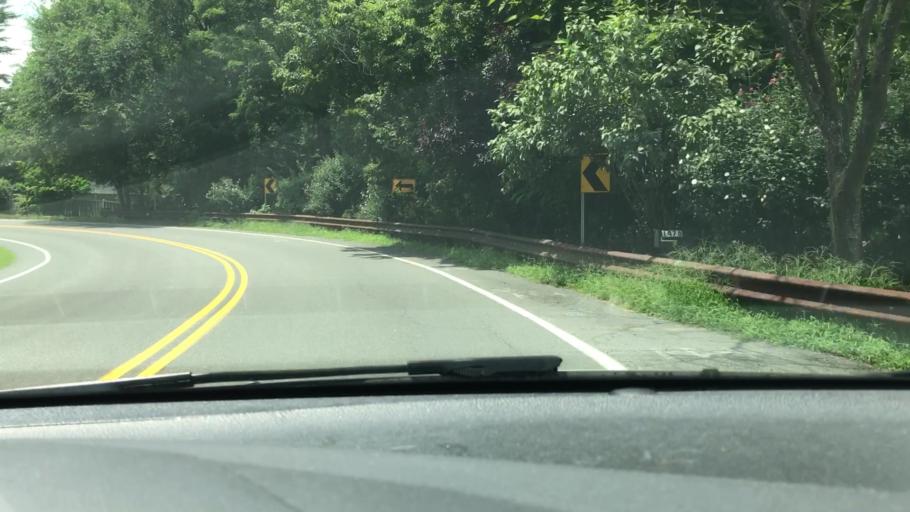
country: US
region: Maryland
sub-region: Montgomery County
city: Brookmont
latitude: 38.9301
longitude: -77.1467
